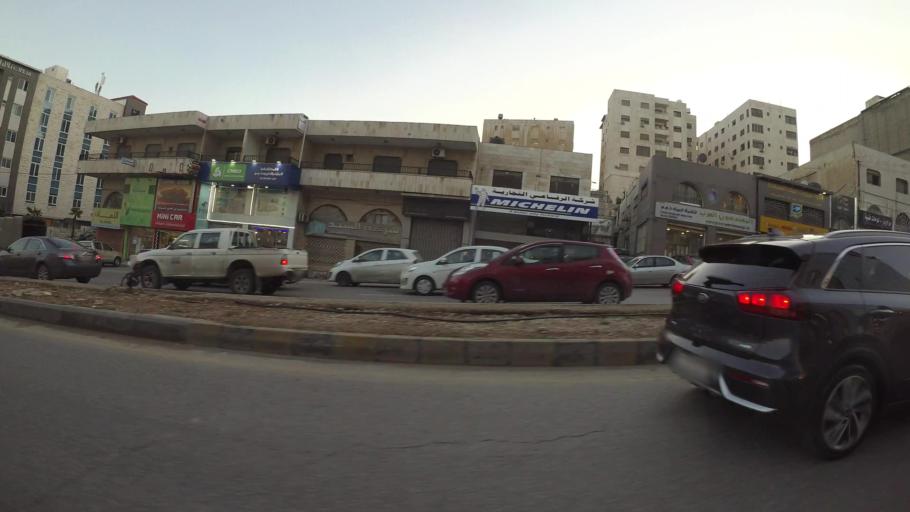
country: JO
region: Amman
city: Al Jubayhah
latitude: 31.9953
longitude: 35.8570
